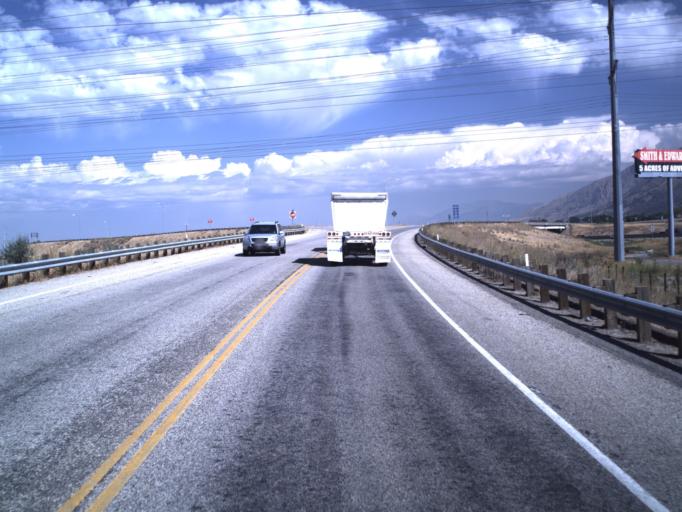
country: US
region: Utah
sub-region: Box Elder County
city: South Willard
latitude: 41.3373
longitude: -112.0375
